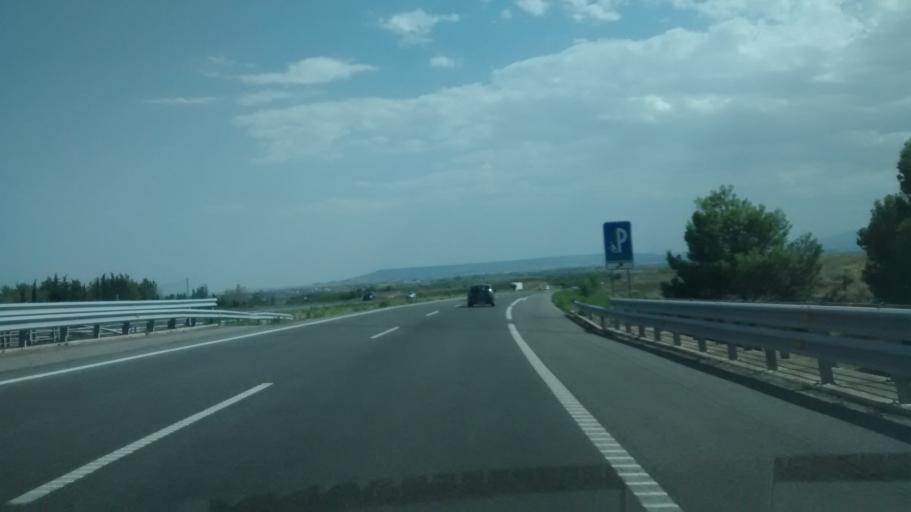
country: ES
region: Navarre
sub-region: Provincia de Navarra
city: Murchante
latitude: 42.0712
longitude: -1.6923
